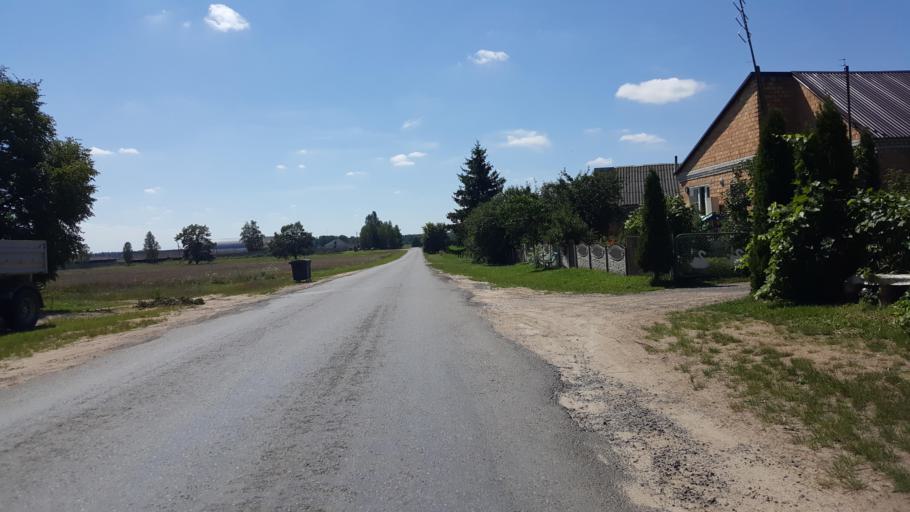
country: BY
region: Brest
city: Charnawchytsy
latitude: 52.3429
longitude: 23.6061
